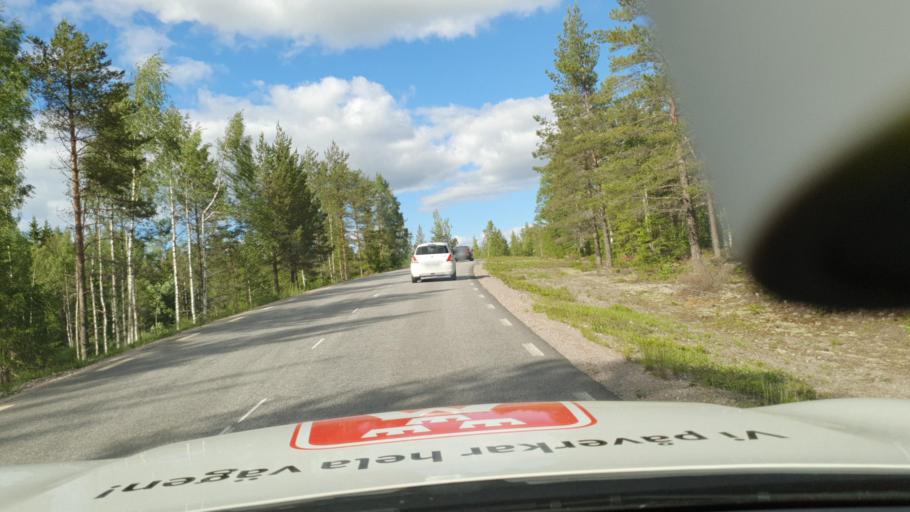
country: SE
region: Vaesterbotten
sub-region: Vannas Kommun
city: Vannasby
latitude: 63.8451
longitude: 19.8723
